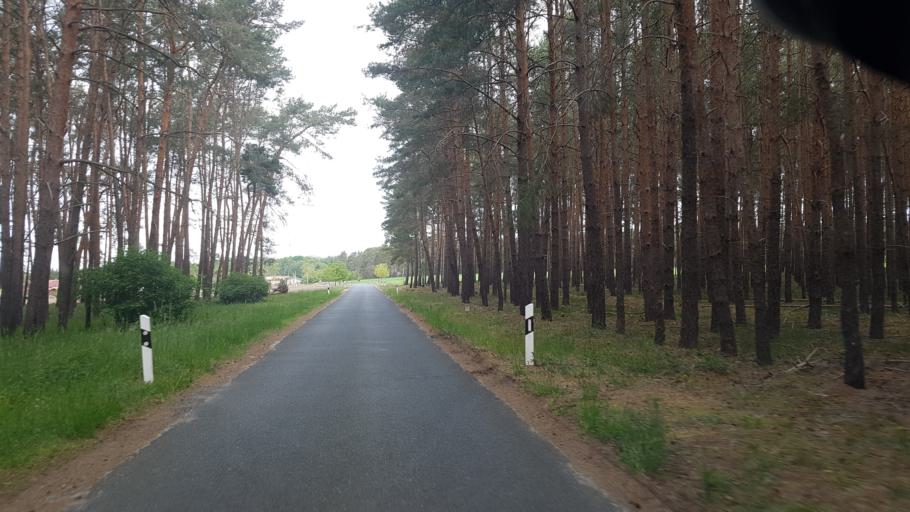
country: DE
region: Brandenburg
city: Luckenwalde
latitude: 52.1248
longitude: 13.0821
